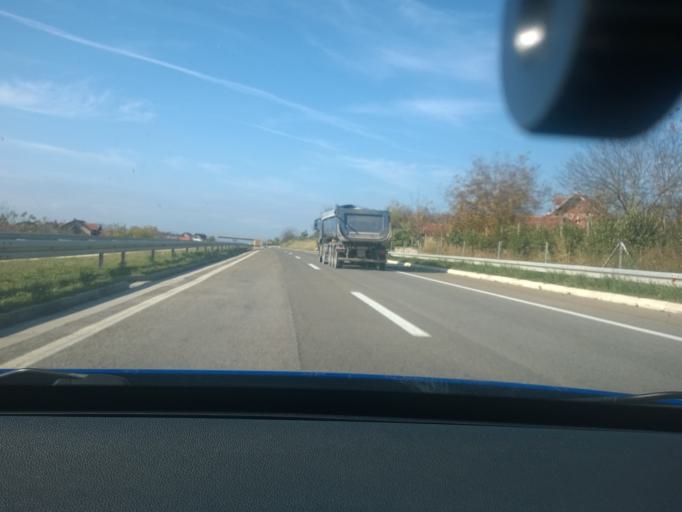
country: RS
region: Central Serbia
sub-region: Nisavski Okrug
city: Nis
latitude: 43.3423
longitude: 21.9188
